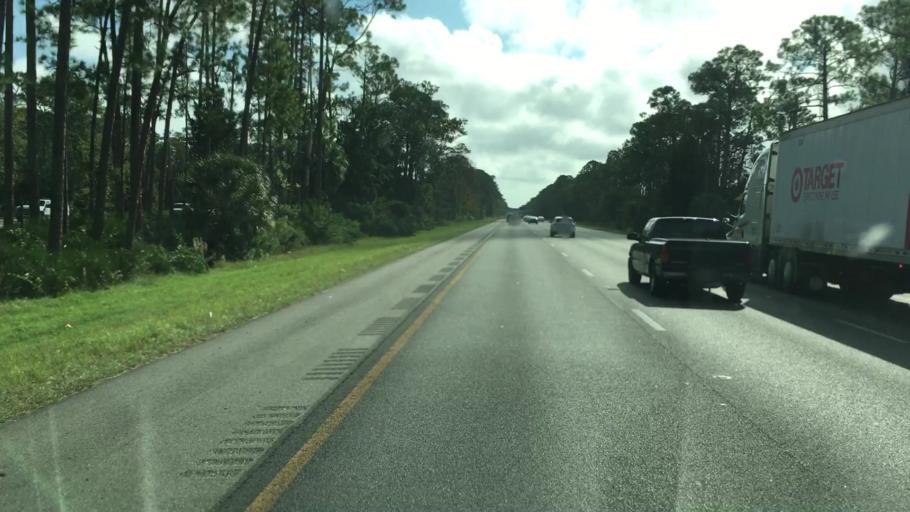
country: US
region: Florida
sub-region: Volusia County
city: Port Orange
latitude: 29.1268
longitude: -81.0556
